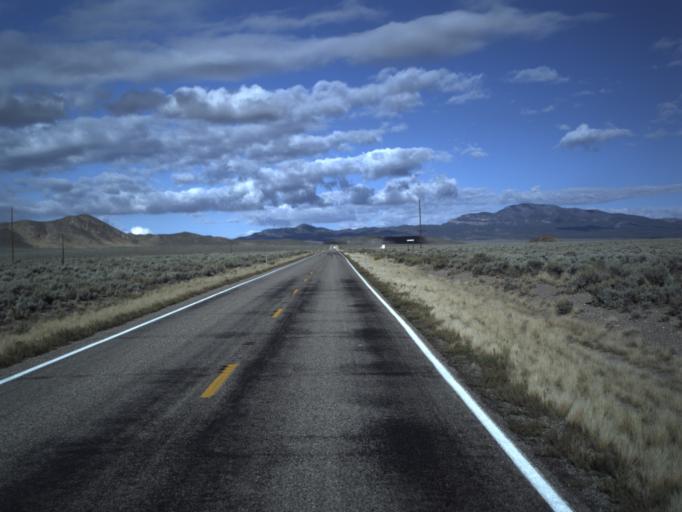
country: US
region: Utah
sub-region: Beaver County
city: Milford
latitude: 38.4129
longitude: -113.0723
